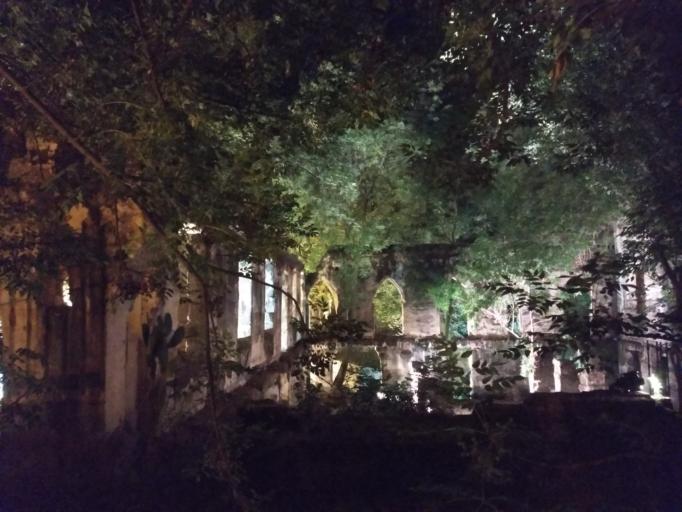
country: MX
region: Jalisco
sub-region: Zapopan
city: Campo Real
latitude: 20.7984
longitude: -103.4371
